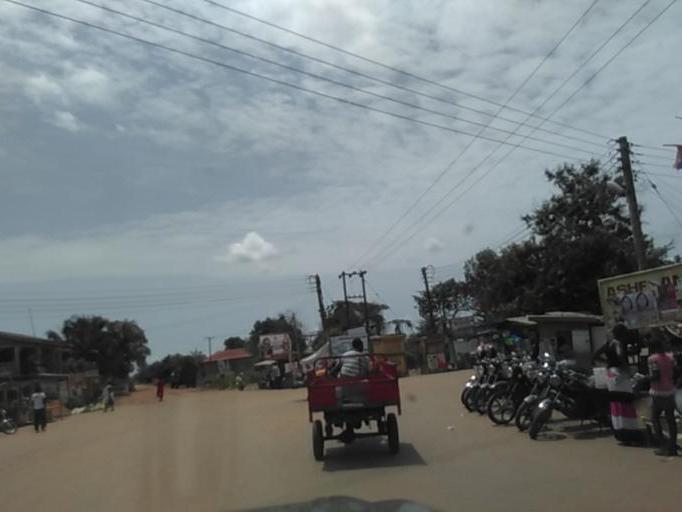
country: GH
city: Akropong
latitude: 6.0915
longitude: 0.1962
